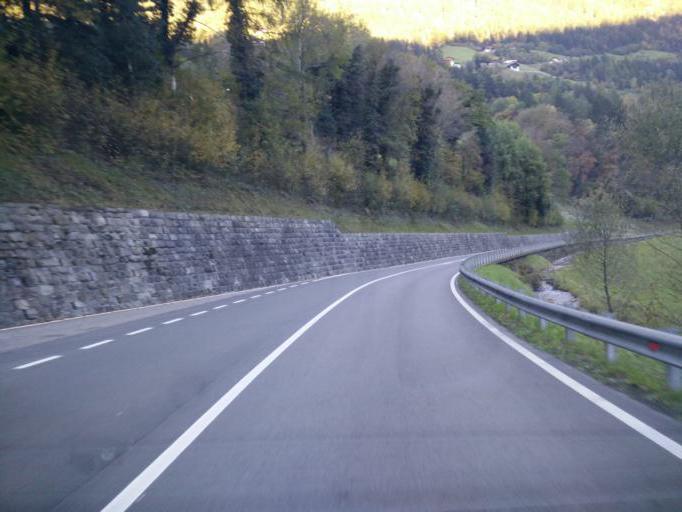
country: IT
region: Trentino-Alto Adige
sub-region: Bolzano
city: San Martino in Passiria
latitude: 46.7486
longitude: 11.2075
